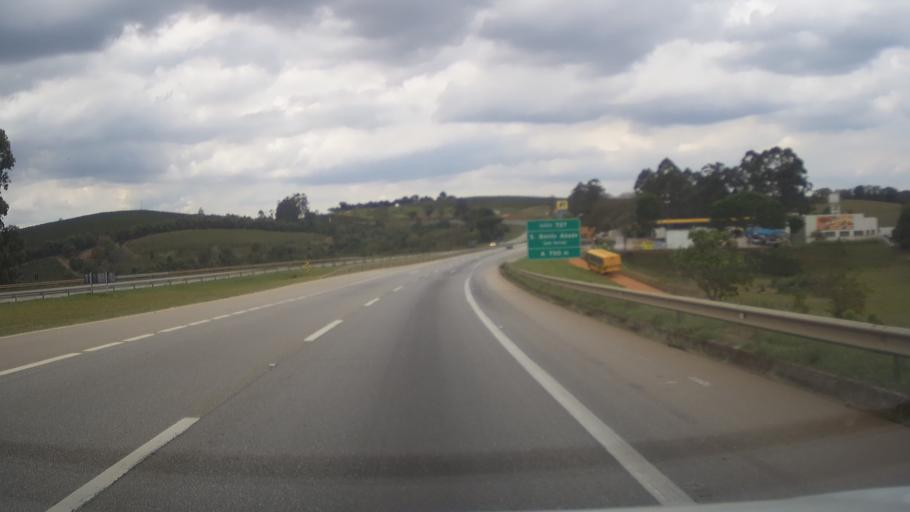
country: BR
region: Minas Gerais
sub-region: Tres Coracoes
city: Tres Coracoes
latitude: -21.4850
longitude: -45.2050
